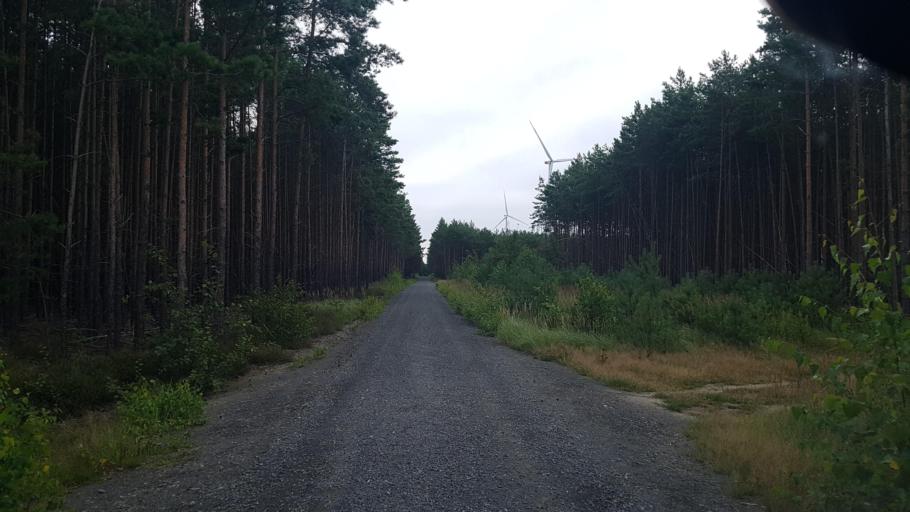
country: DE
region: Brandenburg
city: Grossraschen
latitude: 51.6245
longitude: 13.9828
